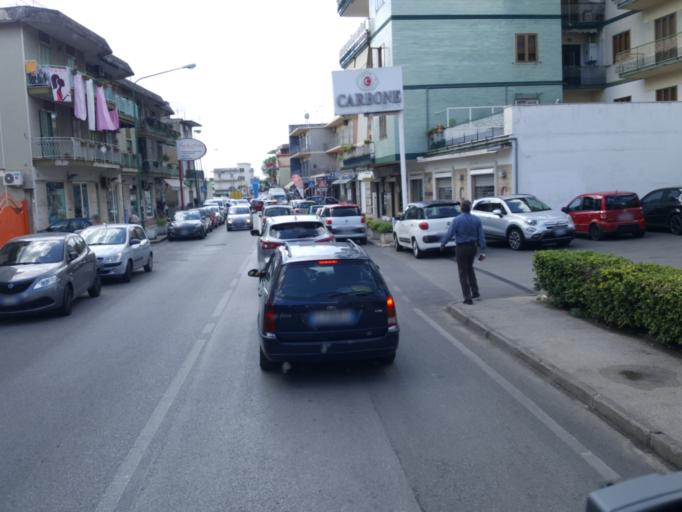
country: IT
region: Campania
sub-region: Provincia di Napoli
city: Nola
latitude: 40.9203
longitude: 14.5348
